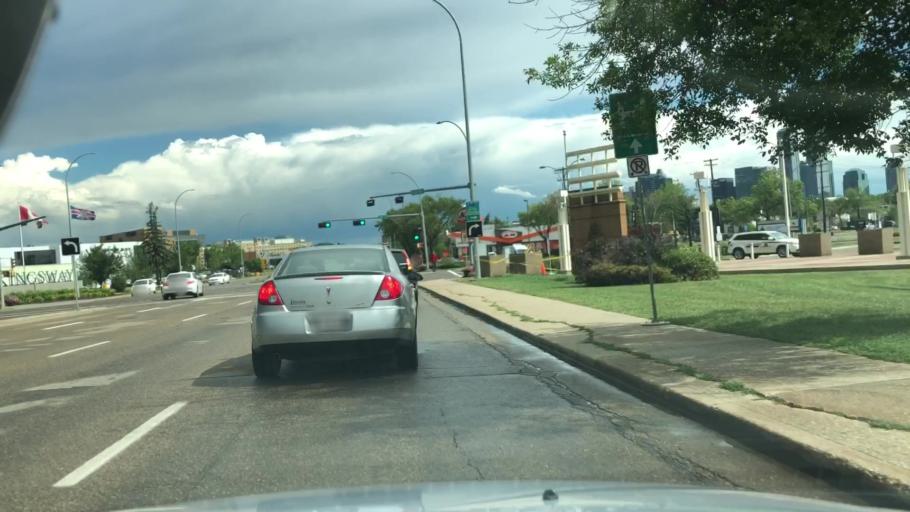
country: CA
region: Alberta
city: Edmonton
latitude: 53.5611
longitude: -113.5092
